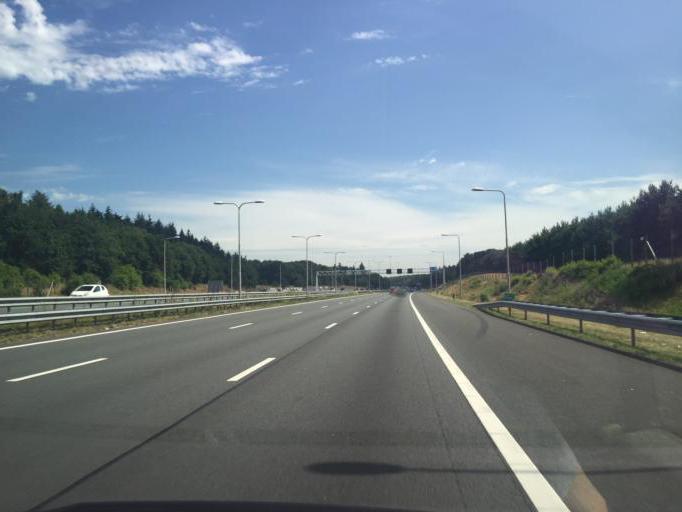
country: NL
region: Gelderland
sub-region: Gemeente Renkum
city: Wolfheze
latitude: 51.9949
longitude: 5.7869
